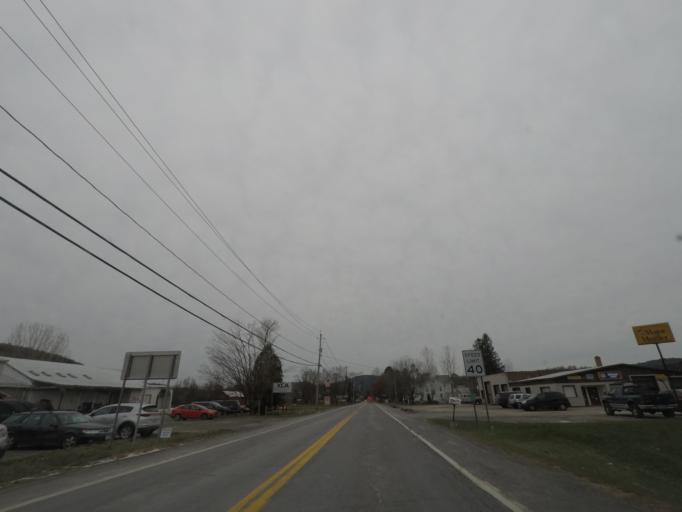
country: US
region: Massachusetts
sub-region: Berkshire County
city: Lanesborough
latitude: 42.5479
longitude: -73.3696
